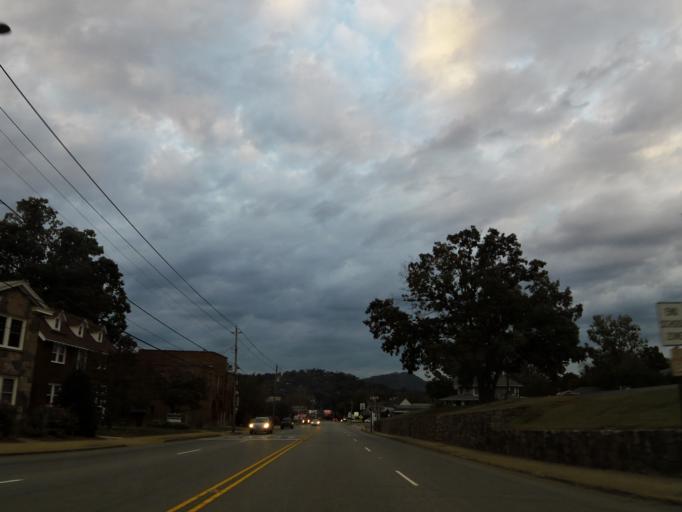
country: US
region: North Carolina
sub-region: Buncombe County
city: Asheville
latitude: 35.6086
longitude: -82.5542
